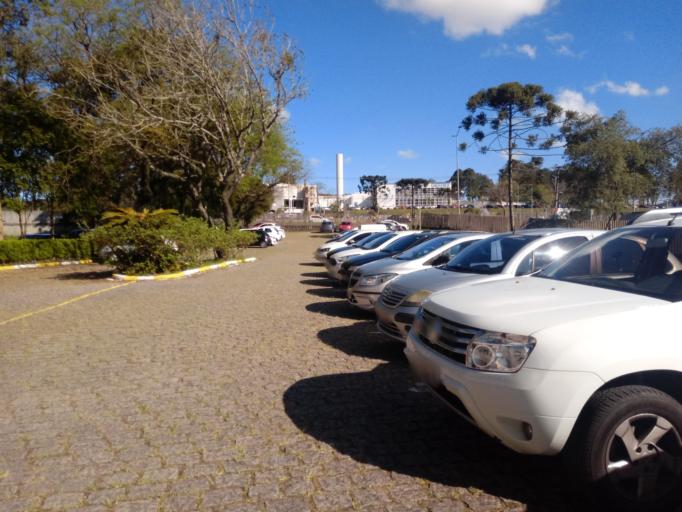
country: BR
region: Parana
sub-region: Curitiba
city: Curitiba
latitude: -25.4510
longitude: -49.2394
